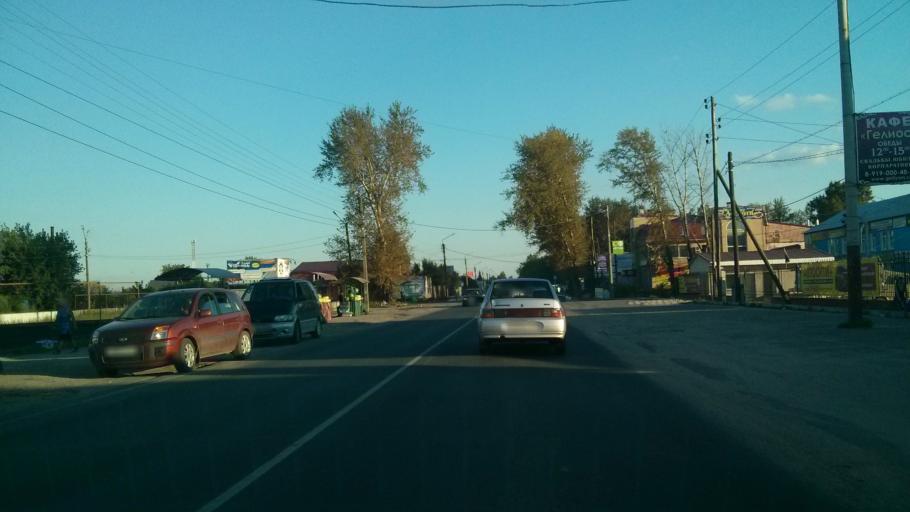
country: RU
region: Vladimir
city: Murom
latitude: 55.5940
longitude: 42.0343
